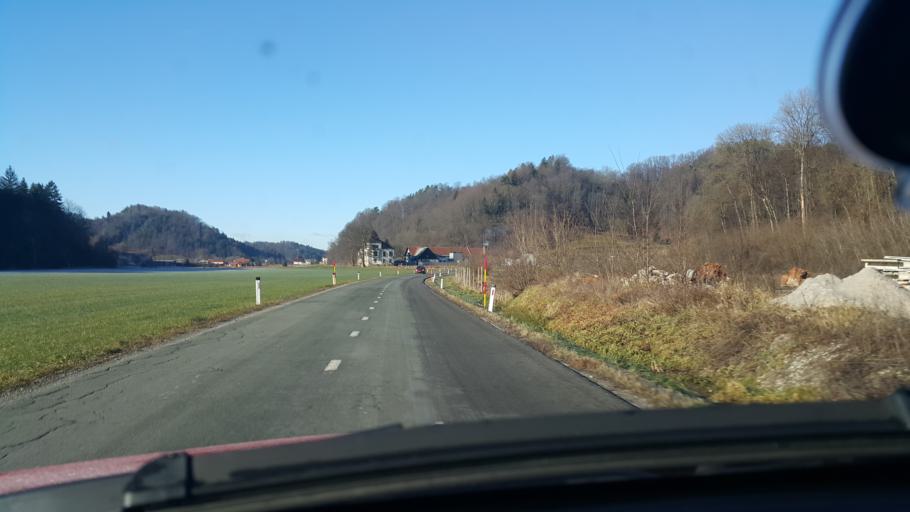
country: SI
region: Kungota
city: Zgornja Kungota
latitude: 46.6380
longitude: 15.6074
